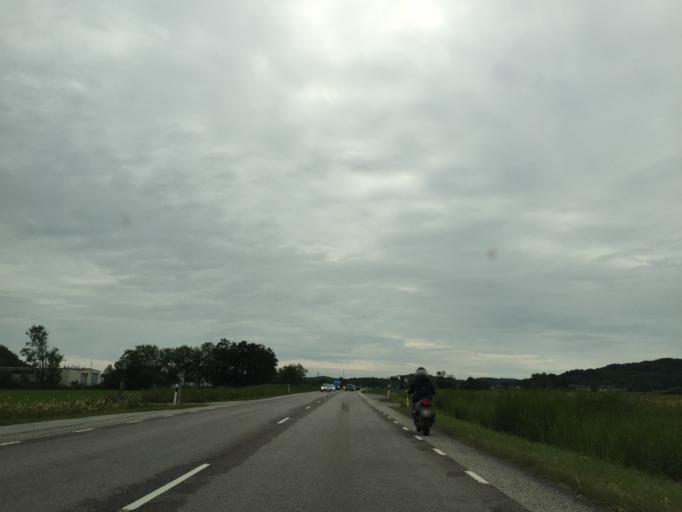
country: SE
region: Vaestra Goetaland
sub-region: Tjorns Kommun
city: Myggenas
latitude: 58.0344
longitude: 11.7268
